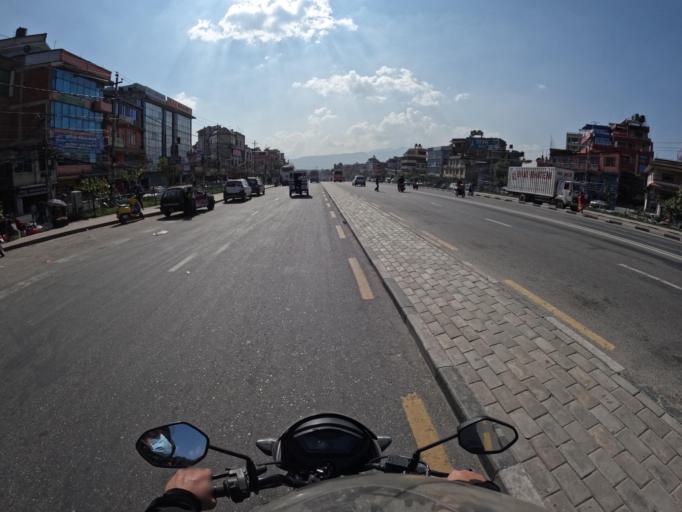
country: NP
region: Central Region
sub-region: Bagmati Zone
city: Patan
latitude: 27.6766
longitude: 85.3462
